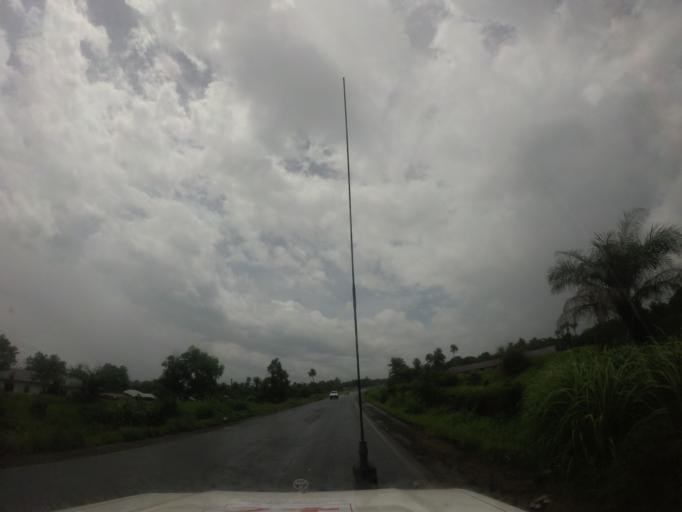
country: SL
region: Northern Province
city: Port Loko
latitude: 8.4880
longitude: -12.7838
